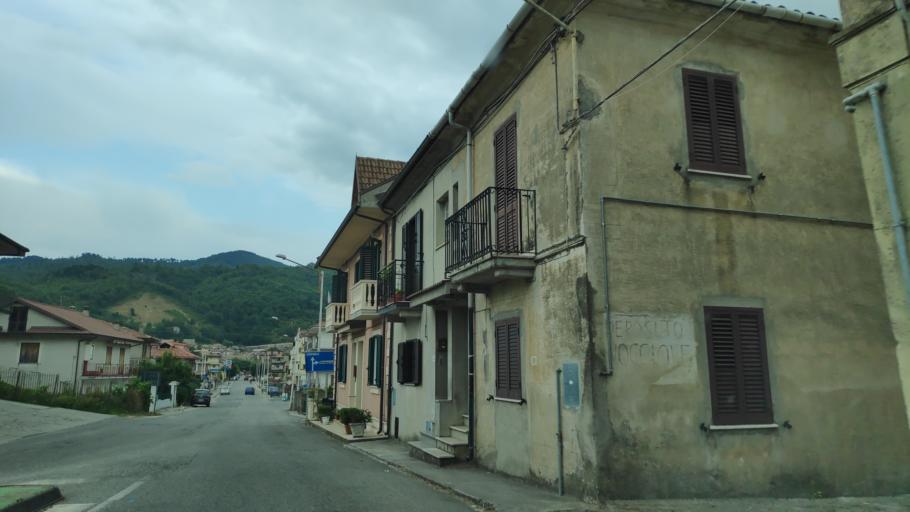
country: IT
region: Calabria
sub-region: Provincia di Catanzaro
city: Cardinale
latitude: 38.6464
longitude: 16.3824
